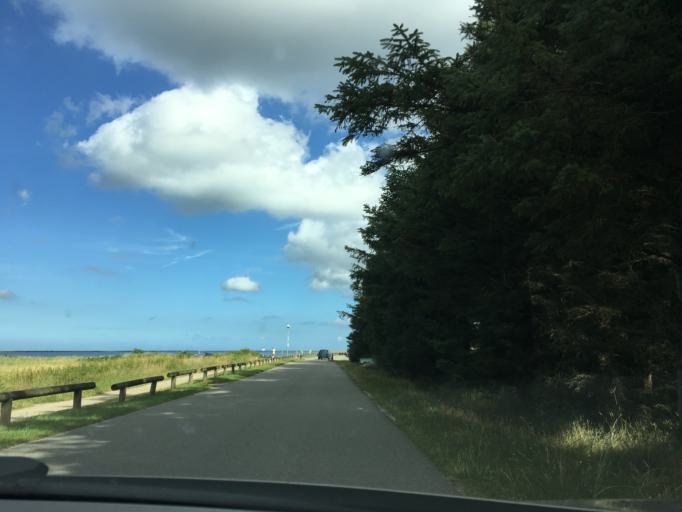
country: DK
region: South Denmark
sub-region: Varde Kommune
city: Oksbol
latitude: 55.8437
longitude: 8.2762
